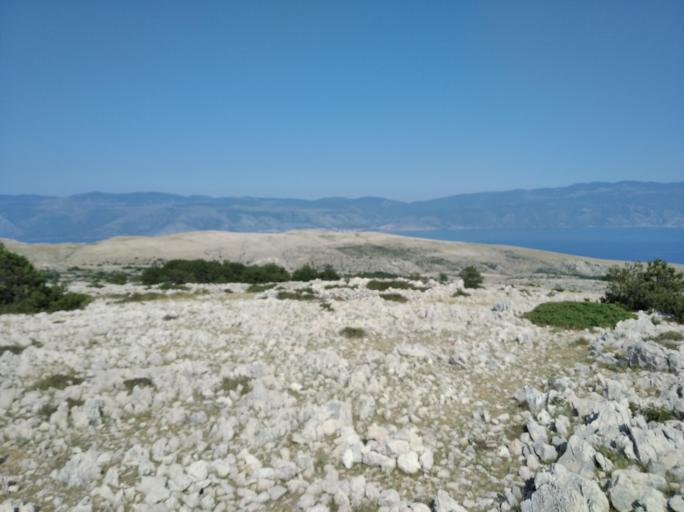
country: HR
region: Primorsko-Goranska
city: Punat
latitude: 44.9813
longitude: 14.7651
